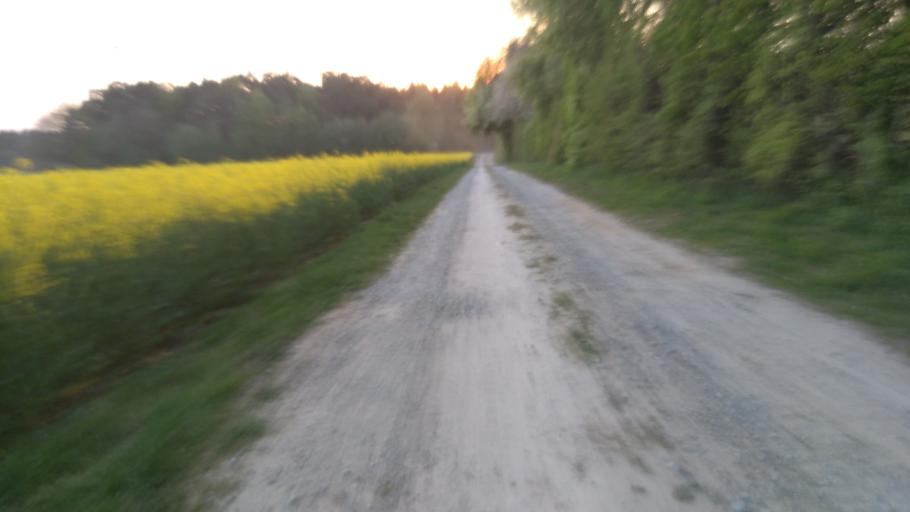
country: DE
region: Lower Saxony
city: Harsefeld
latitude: 53.4943
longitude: 9.5029
